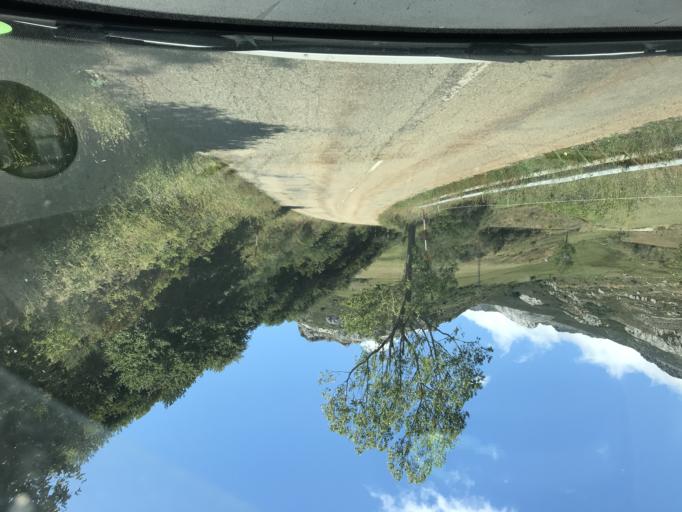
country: ES
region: Castille and Leon
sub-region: Provincia de Palencia
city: Polentinos
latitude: 43.0341
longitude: -4.4587
